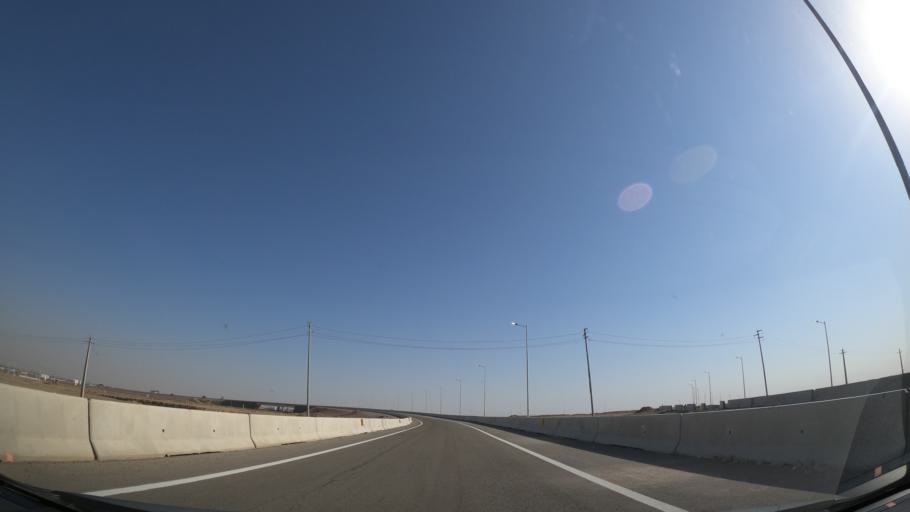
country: IR
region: Tehran
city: Eqbaliyeh
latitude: 35.1351
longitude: 51.5084
